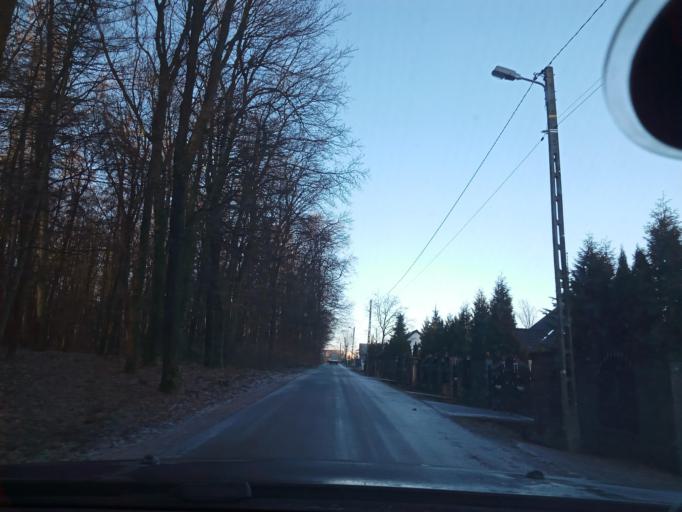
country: PL
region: Lesser Poland Voivodeship
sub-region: Powiat krakowski
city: Michalowice
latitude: 50.1978
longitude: 20.0124
